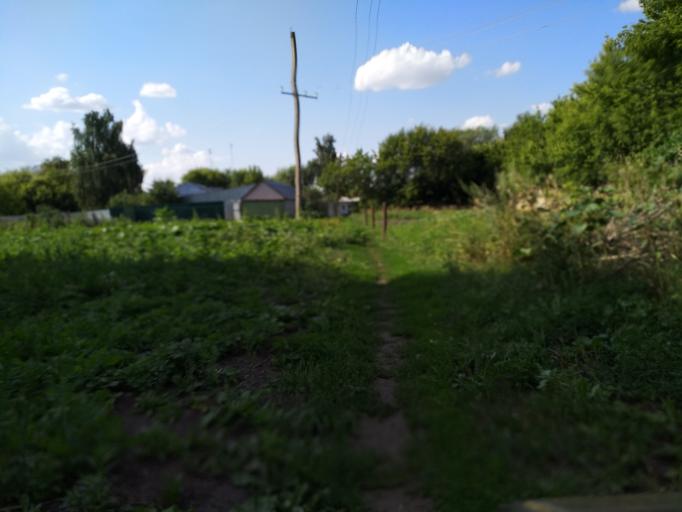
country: RU
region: Lipetsk
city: Dobrinka
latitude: 52.0390
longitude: 40.5496
